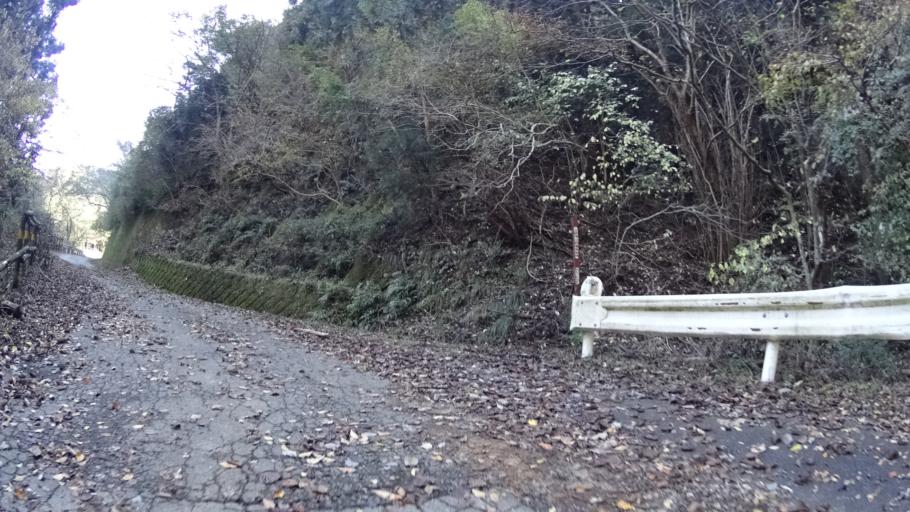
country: JP
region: Kanagawa
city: Atsugi
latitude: 35.5093
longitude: 139.2669
